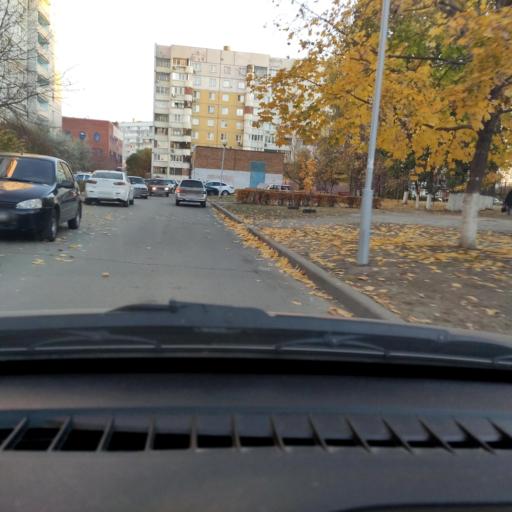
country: RU
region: Samara
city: Tol'yatti
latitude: 53.5394
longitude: 49.3462
